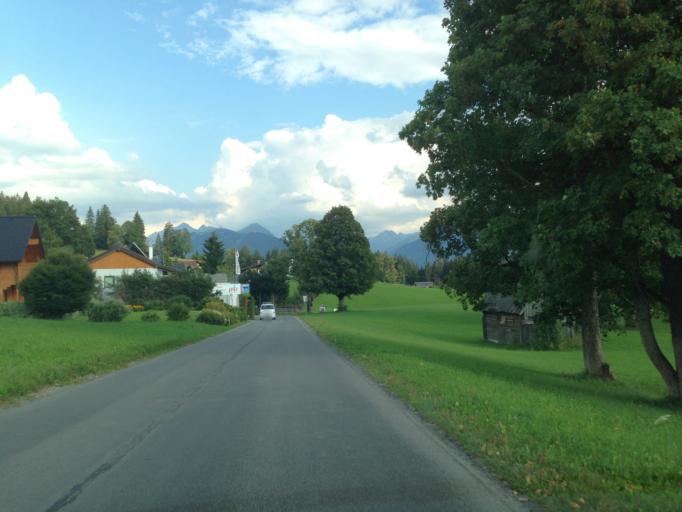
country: AT
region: Styria
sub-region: Politischer Bezirk Liezen
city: Schladming
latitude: 47.4117
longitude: 13.6349
